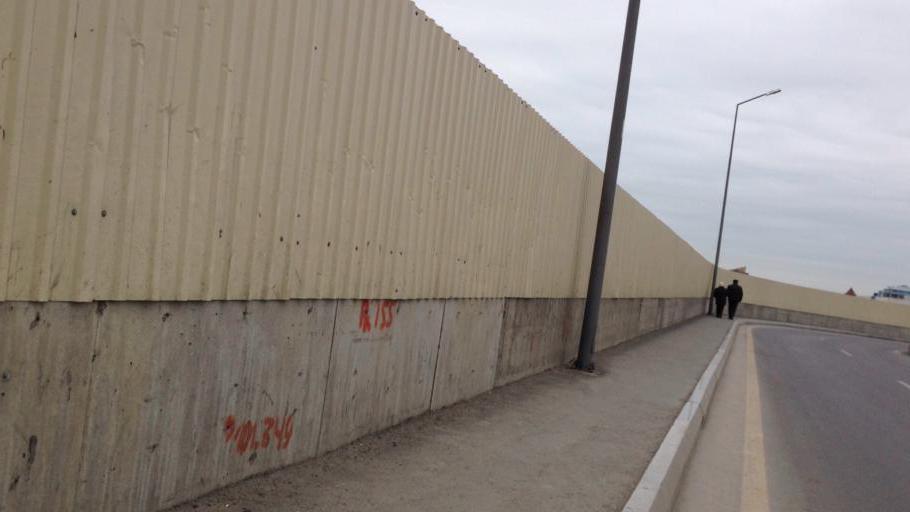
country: AZ
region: Baki
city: Baku
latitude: 40.3983
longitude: 49.8498
